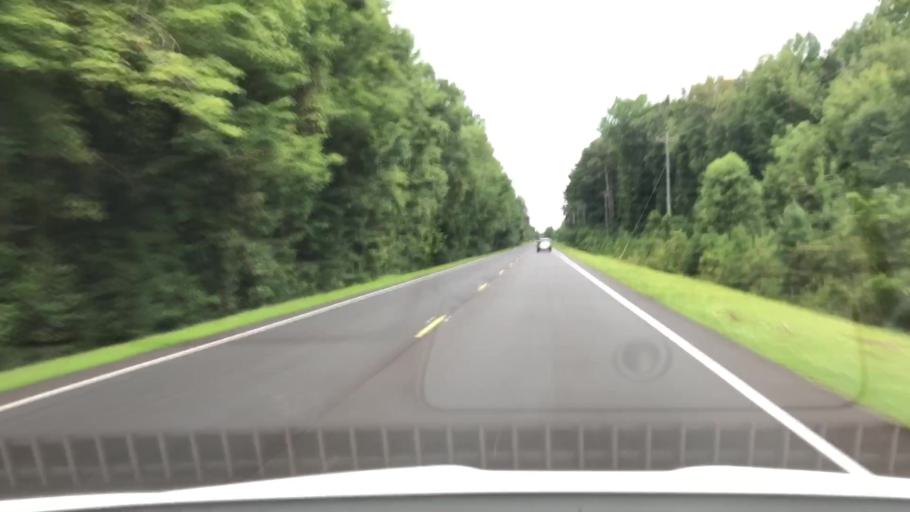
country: US
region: North Carolina
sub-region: Jones County
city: Maysville
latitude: 34.8732
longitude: -77.1981
